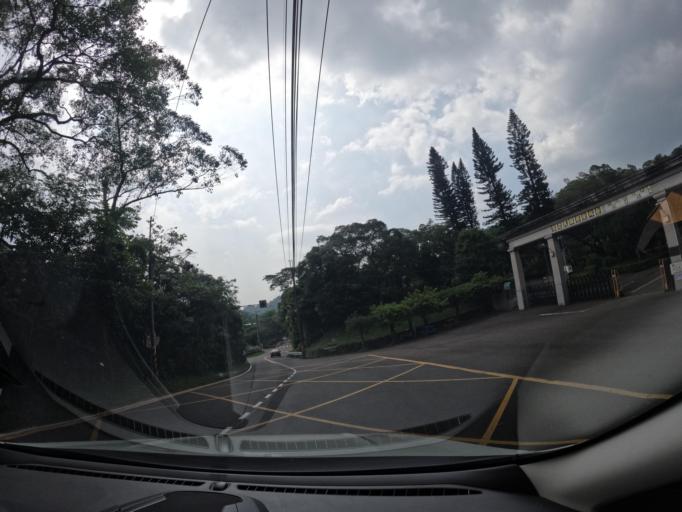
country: TW
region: Taiwan
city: Daxi
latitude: 24.9098
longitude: 121.3926
